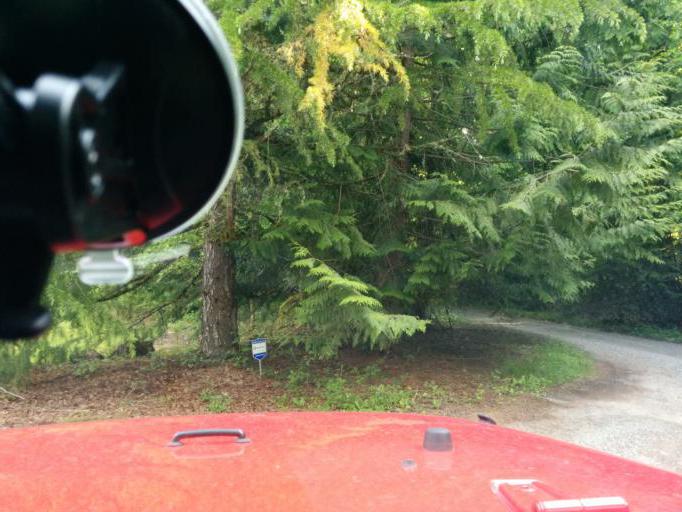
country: US
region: Washington
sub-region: King County
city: Union Hill-Novelty Hill
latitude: 47.6710
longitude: -122.0172
